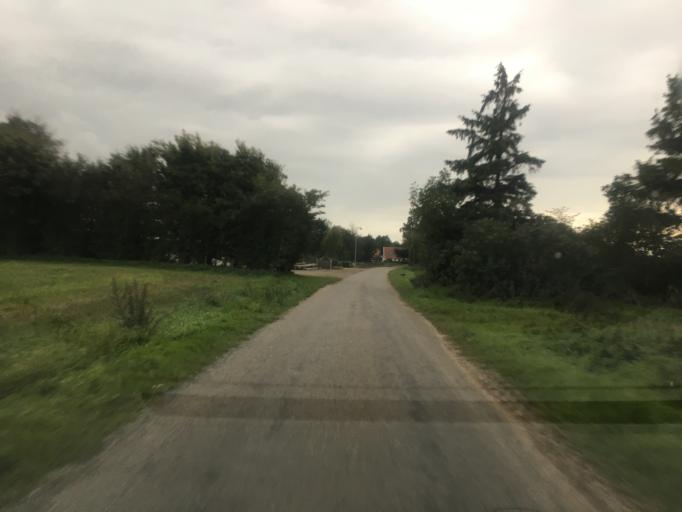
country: DE
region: Schleswig-Holstein
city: Ellhoft
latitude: 54.9628
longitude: 9.0159
